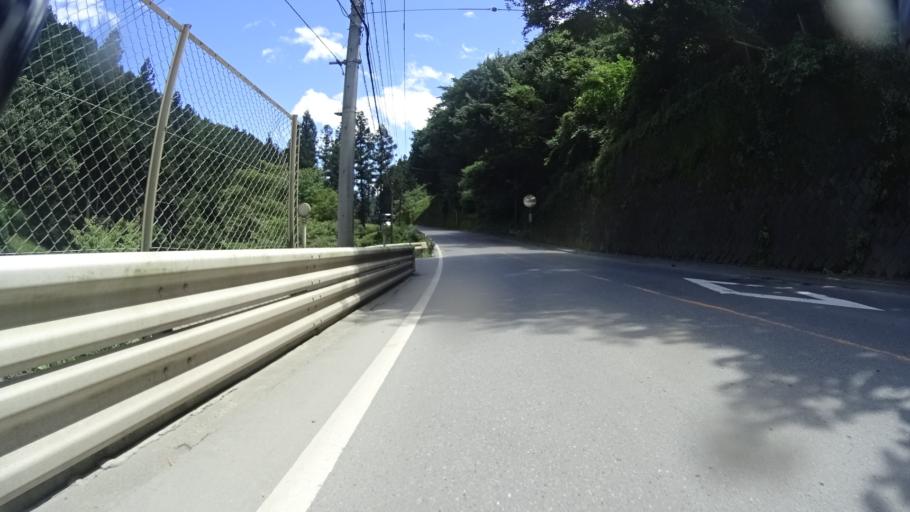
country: JP
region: Tokyo
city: Ome
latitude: 35.8204
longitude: 139.2325
